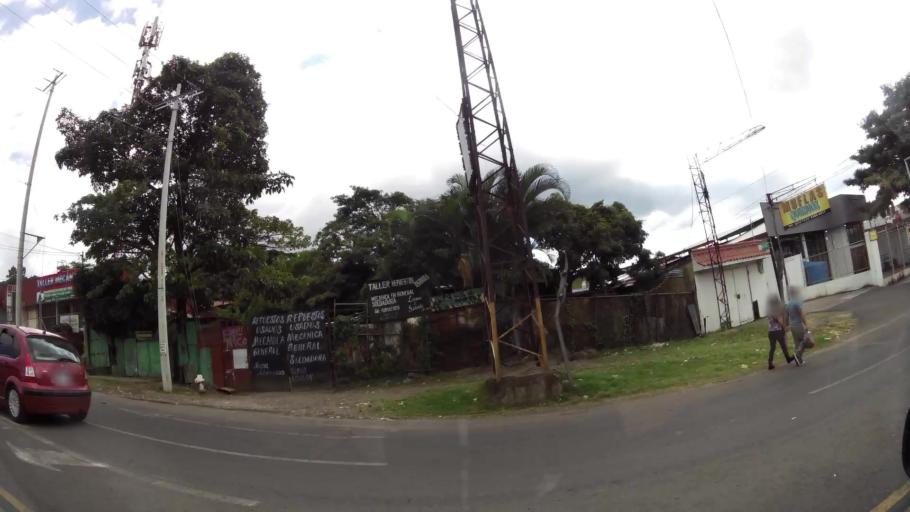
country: CR
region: San Jose
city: San Rafael
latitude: 9.9495
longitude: -84.1428
